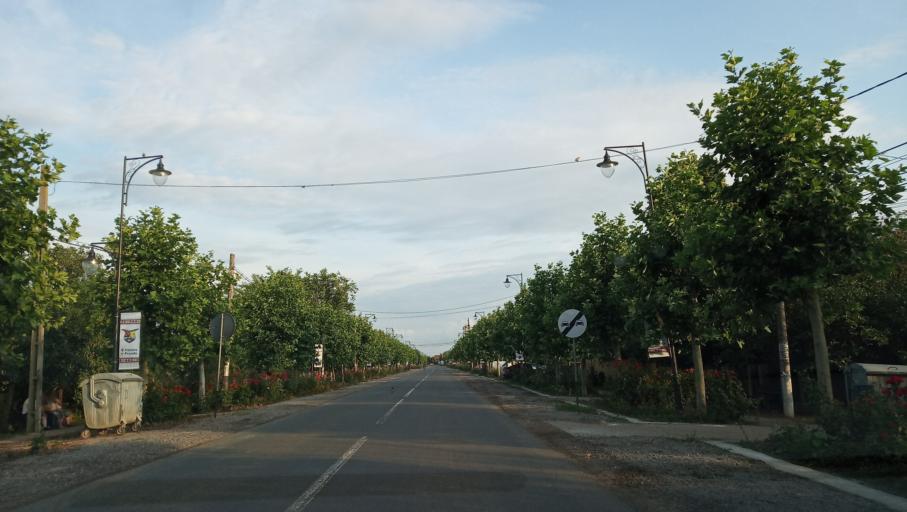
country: RO
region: Giurgiu
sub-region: Comuna Prundu
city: Prundu
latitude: 44.0998
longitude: 26.2274
